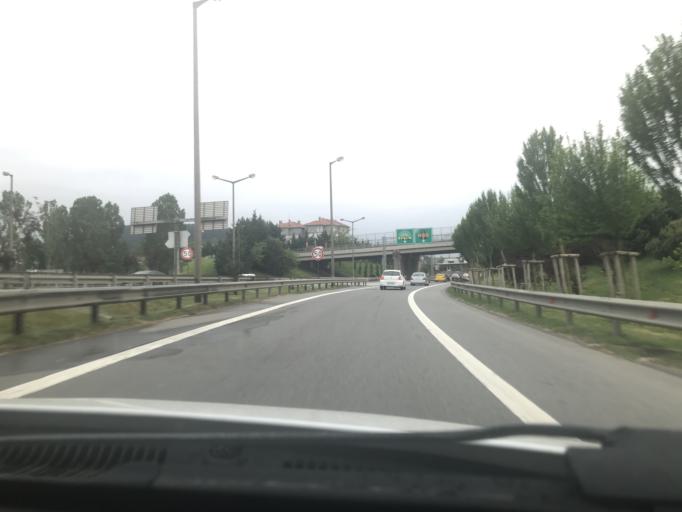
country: TR
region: Istanbul
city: Sultanbeyli
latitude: 40.9354
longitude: 29.3313
